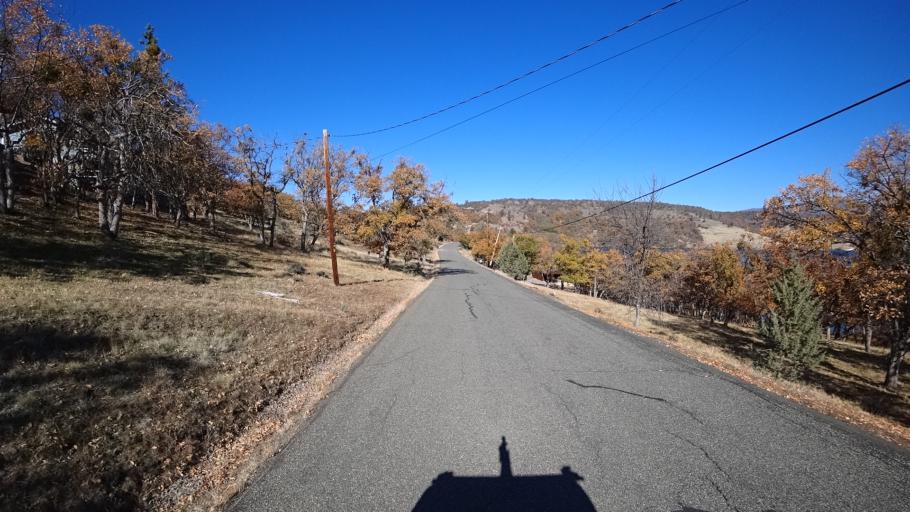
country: US
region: California
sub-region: Siskiyou County
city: Montague
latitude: 41.9762
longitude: -122.3226
